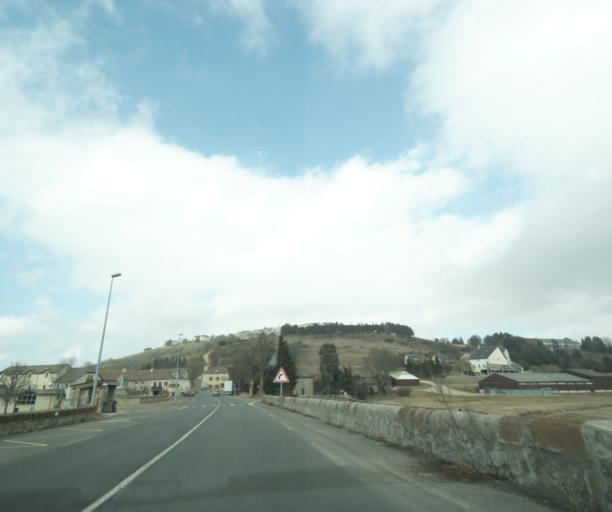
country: FR
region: Languedoc-Roussillon
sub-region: Departement de la Lozere
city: Langogne
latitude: 44.6329
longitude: 3.6762
